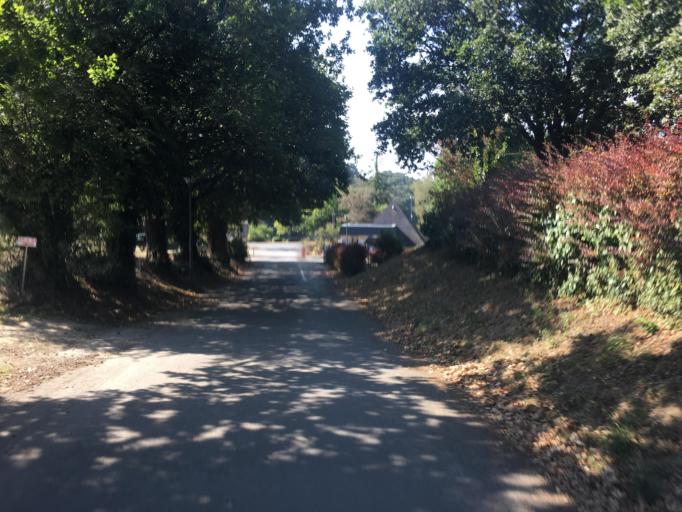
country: FR
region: Brittany
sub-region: Departement des Cotes-d'Armor
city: Mur-de-Bretagne
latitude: 48.1994
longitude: -3.0127
